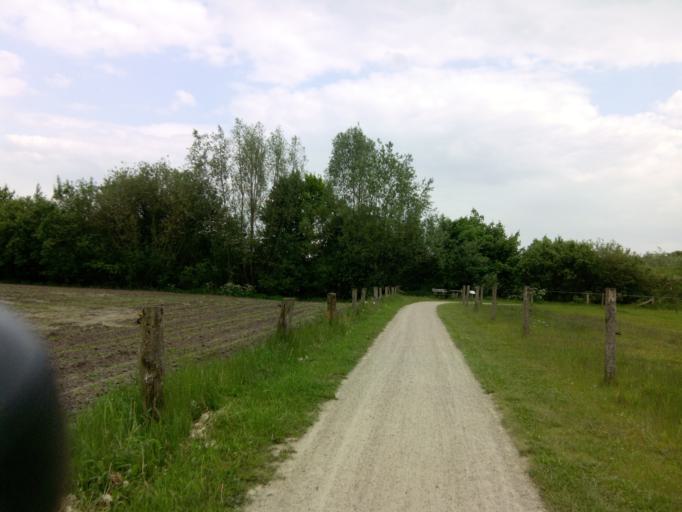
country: NL
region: Gelderland
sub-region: Berkelland
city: Borculo
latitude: 52.0734
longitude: 6.5214
